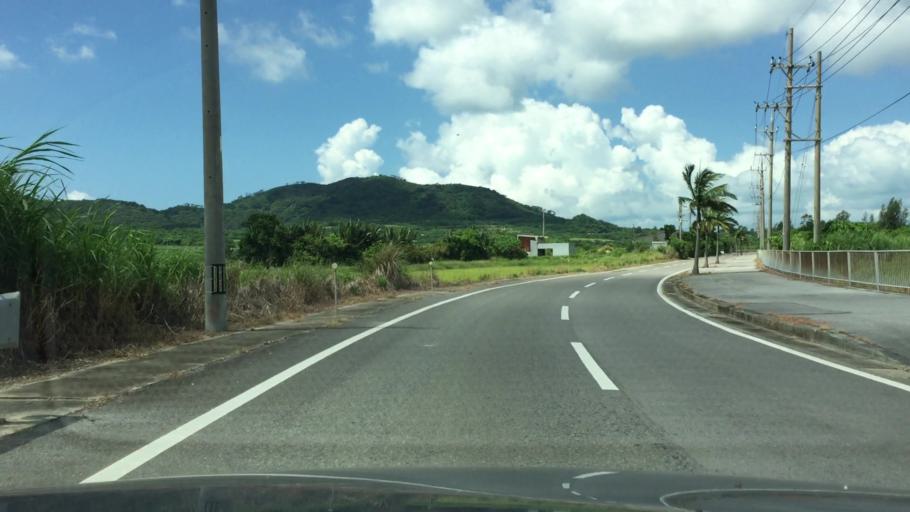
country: JP
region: Okinawa
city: Ishigaki
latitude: 24.3902
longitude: 124.1504
